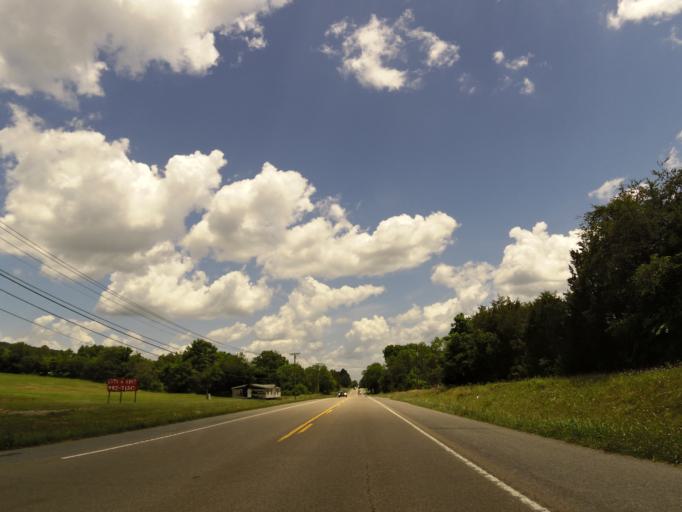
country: US
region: Tennessee
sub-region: Union County
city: Condon
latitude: 36.2109
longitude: -83.8688
